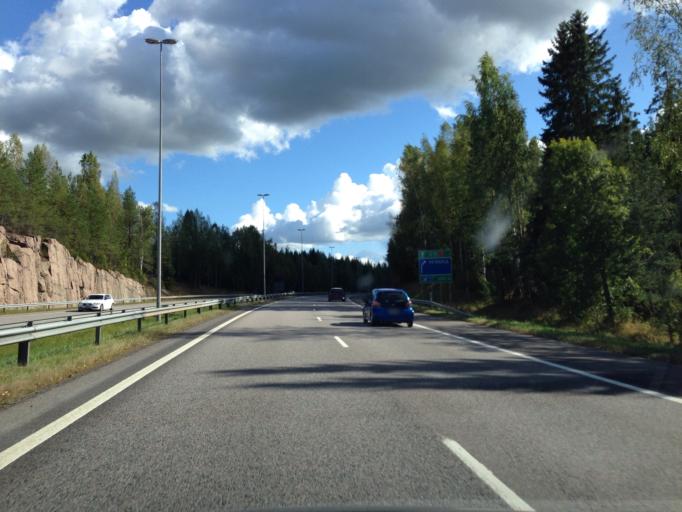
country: FI
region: Uusimaa
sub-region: Helsinki
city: Kirkkonummi
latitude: 60.2801
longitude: 24.4457
